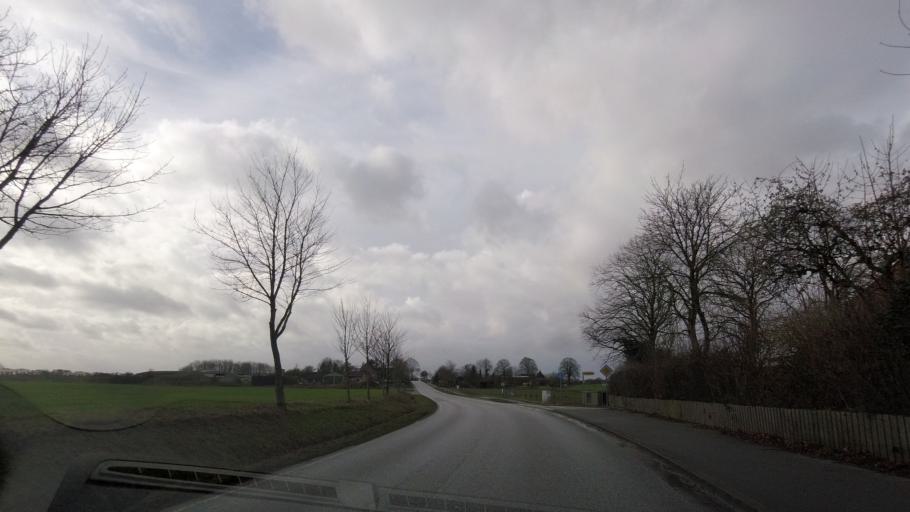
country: DE
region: Schleswig-Holstein
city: Dollrottfeld
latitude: 54.6430
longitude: 9.8045
